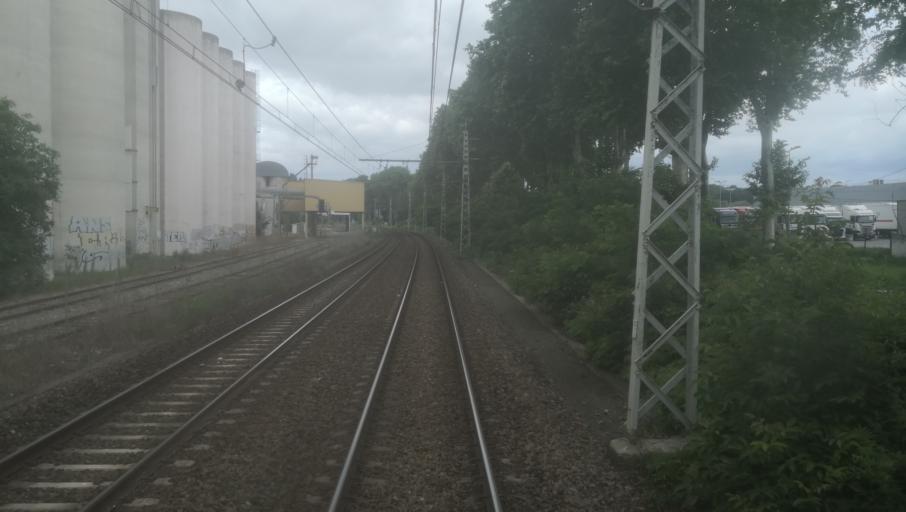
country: FR
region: Midi-Pyrenees
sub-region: Departement de la Haute-Garonne
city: Baziege
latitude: 43.4504
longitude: 1.6282
